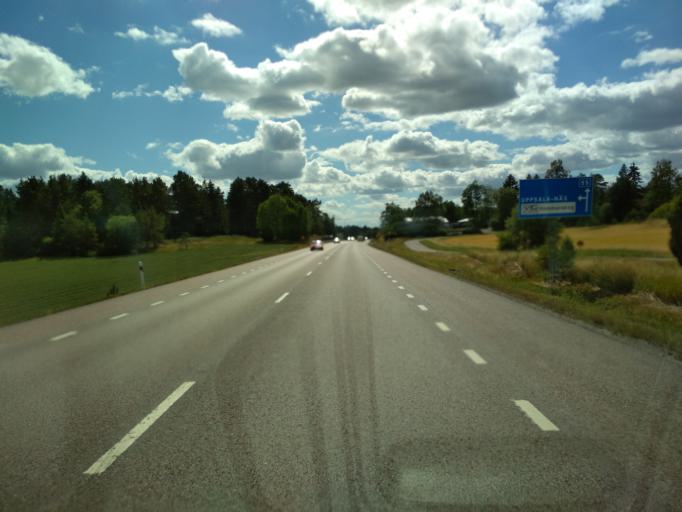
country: SE
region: Uppsala
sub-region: Uppsala Kommun
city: Uppsala
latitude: 59.8220
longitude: 17.4962
